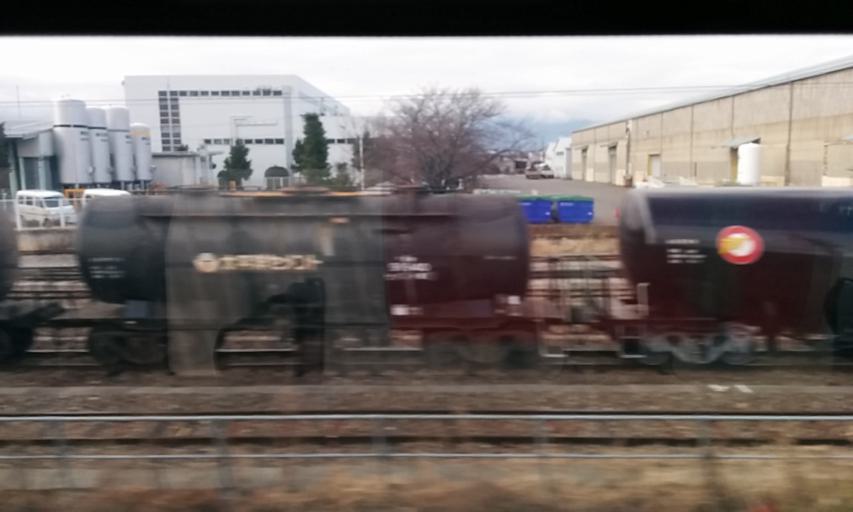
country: JP
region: Nagano
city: Matsumoto
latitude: 36.1987
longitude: 137.9651
